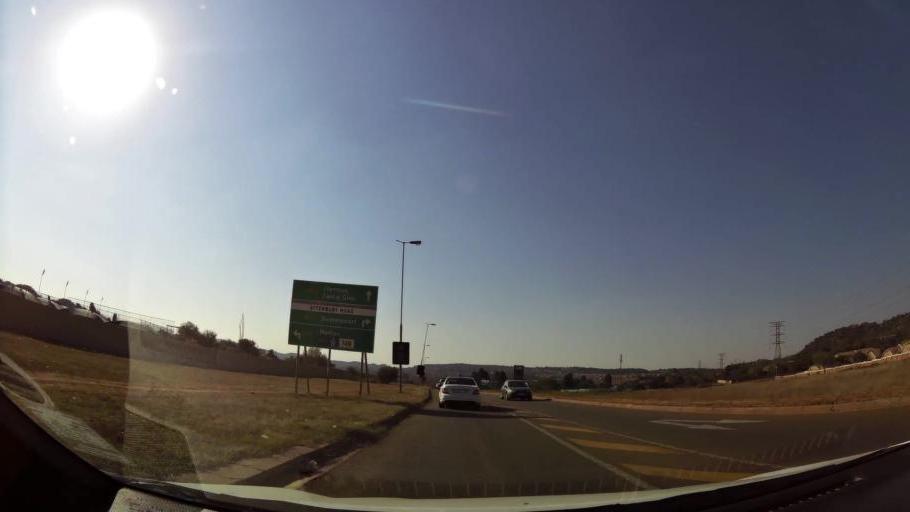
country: ZA
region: Gauteng
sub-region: City of Tshwane Metropolitan Municipality
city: Centurion
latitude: -25.8109
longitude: 28.3282
